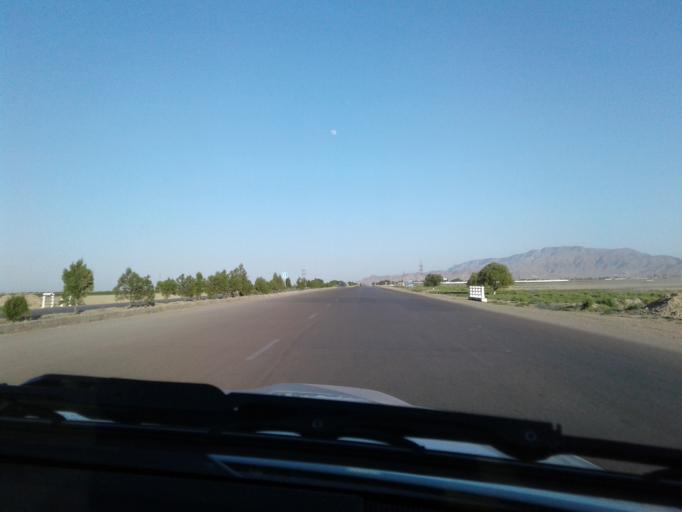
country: TM
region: Ahal
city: Baharly
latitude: 38.3311
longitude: 57.5791
